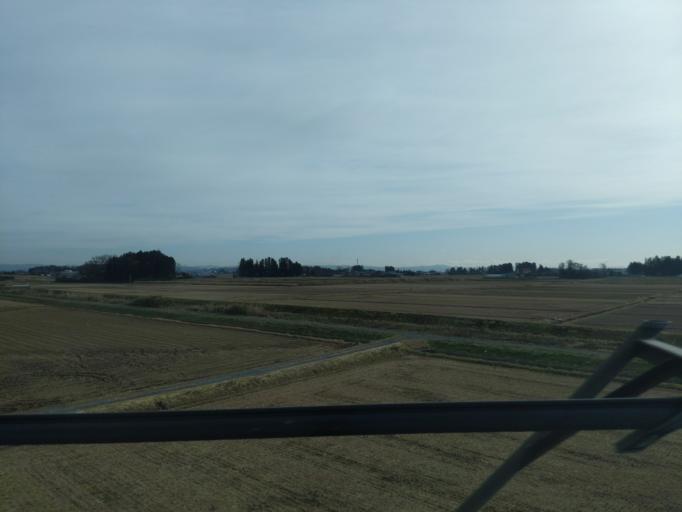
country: JP
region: Iwate
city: Ichinoseki
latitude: 38.7757
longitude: 141.0870
